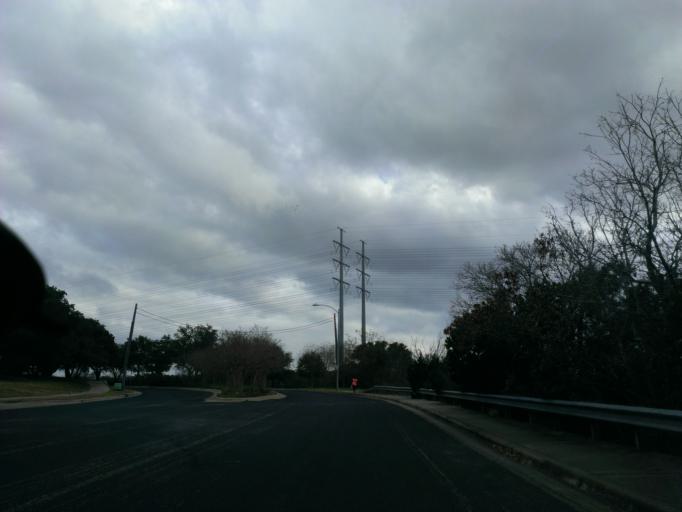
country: US
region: Texas
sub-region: Travis County
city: Wells Branch
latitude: 30.3909
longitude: -97.6744
